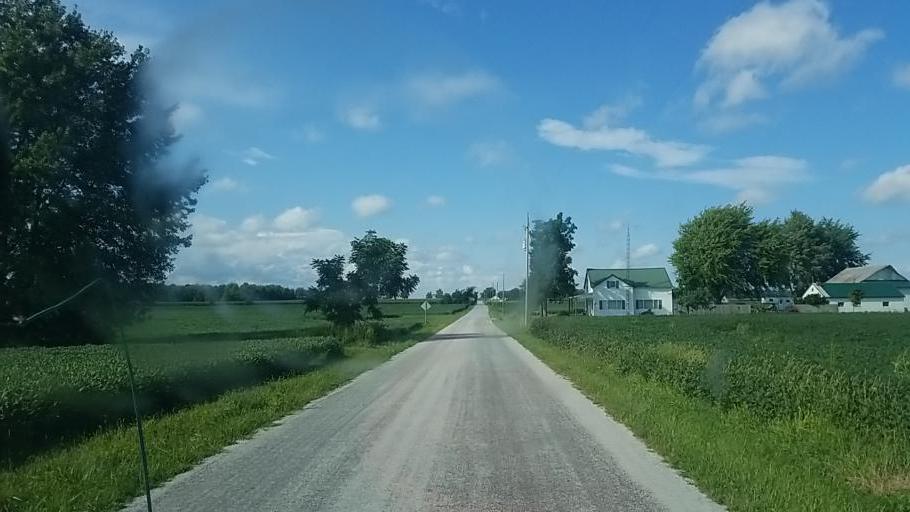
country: US
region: Ohio
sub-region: Hardin County
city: Kenton
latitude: 40.6748
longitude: -83.5311
